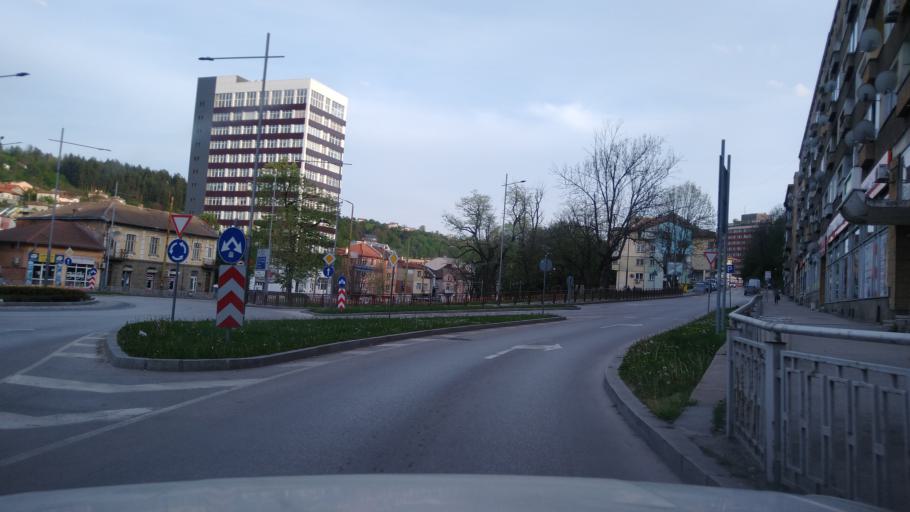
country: BG
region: Gabrovo
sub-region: Obshtina Gabrovo
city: Gabrovo
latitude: 42.8775
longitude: 25.3165
